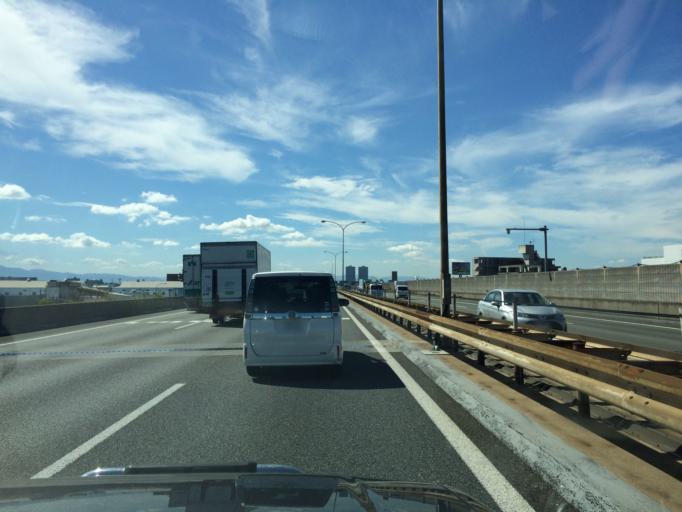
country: JP
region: Osaka
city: Yao
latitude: 34.6522
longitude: 135.5977
